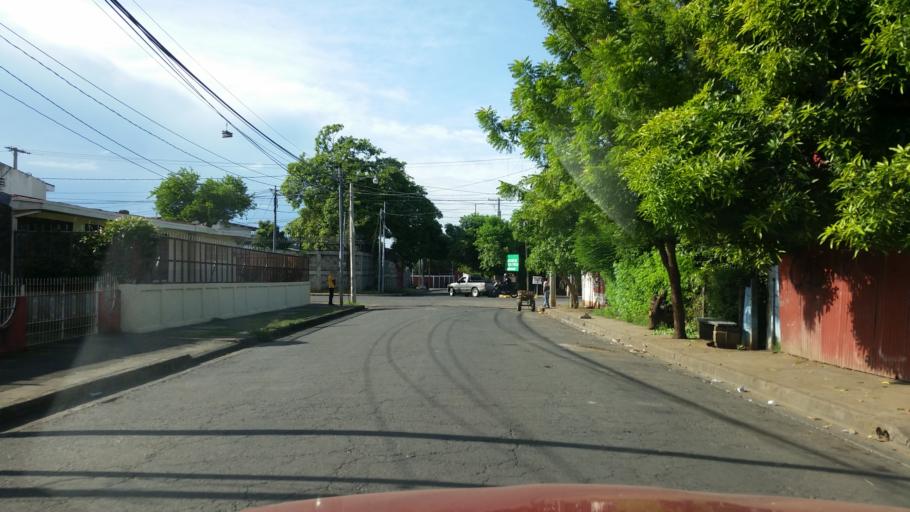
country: NI
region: Managua
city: Managua
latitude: 12.1417
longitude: -86.2640
